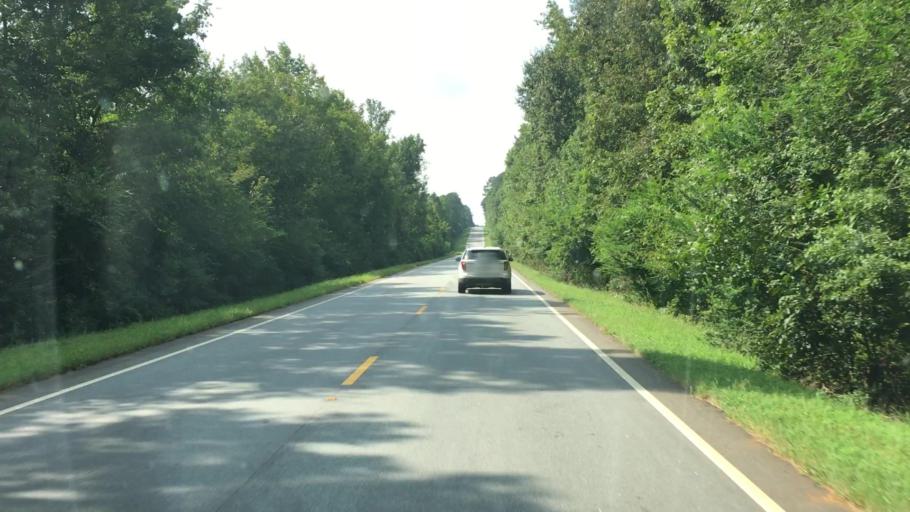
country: US
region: Georgia
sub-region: Jasper County
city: Monticello
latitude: 33.3198
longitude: -83.6966
